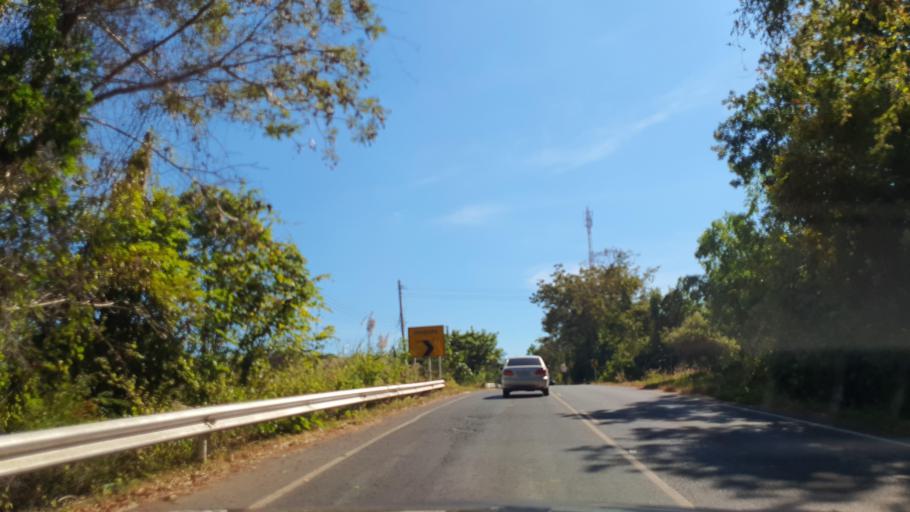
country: TH
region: Kalasin
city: Khao Wong
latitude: 16.7704
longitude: 104.1543
